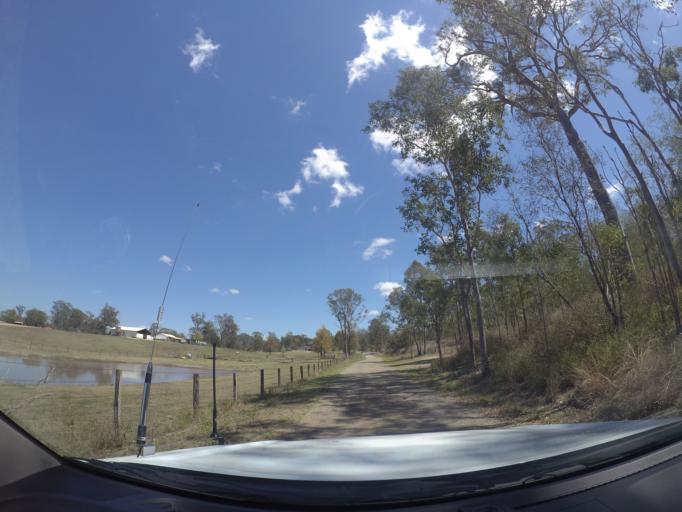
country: AU
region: Queensland
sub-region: Logan
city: Cedar Vale
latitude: -27.8516
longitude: 152.8962
